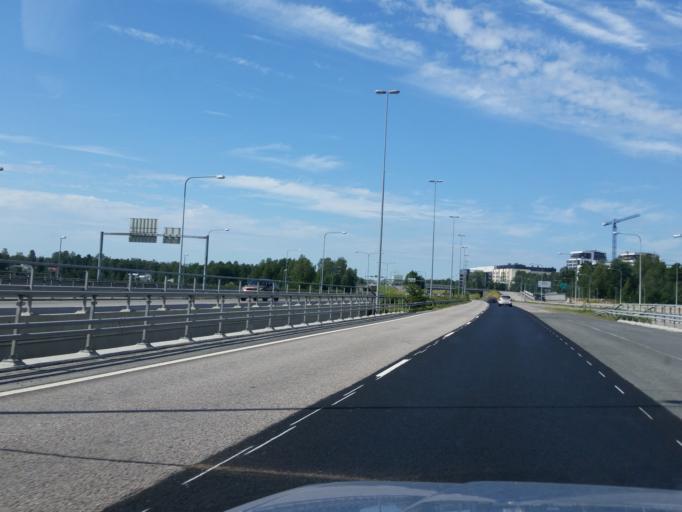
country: FI
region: Uusimaa
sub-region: Helsinki
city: Otaniemi
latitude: 60.1696
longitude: 24.8200
